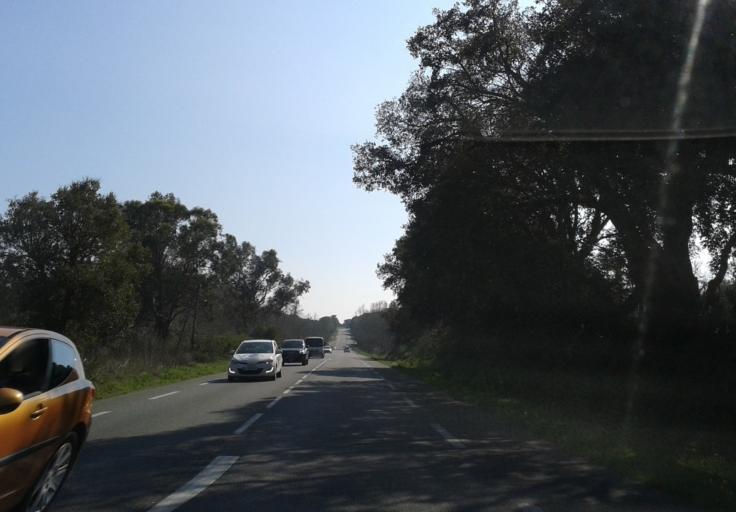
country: FR
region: Corsica
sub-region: Departement de la Haute-Corse
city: Linguizzetta
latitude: 42.2339
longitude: 9.5451
